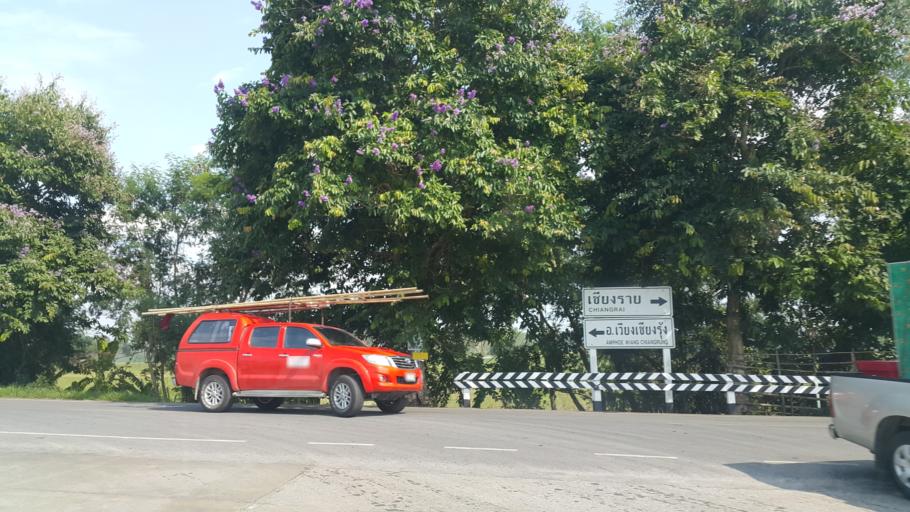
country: TH
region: Chiang Rai
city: Wiang Chai
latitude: 19.9595
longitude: 99.9465
